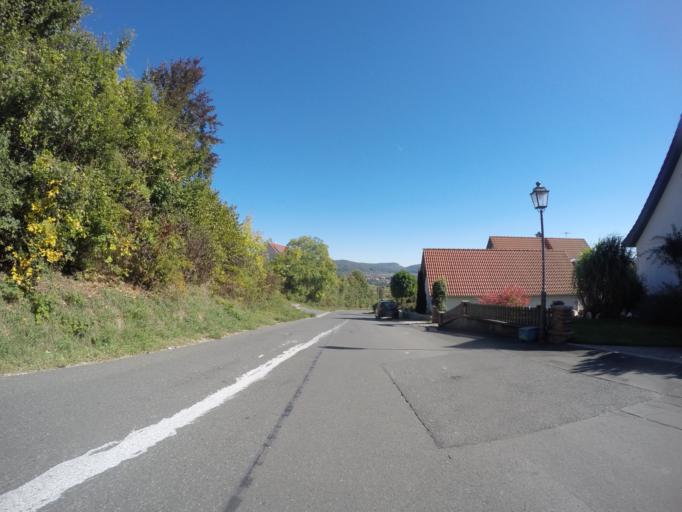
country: DE
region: Bavaria
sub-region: Upper Franconia
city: Kirchehrenbach
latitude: 49.7567
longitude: 11.1419
